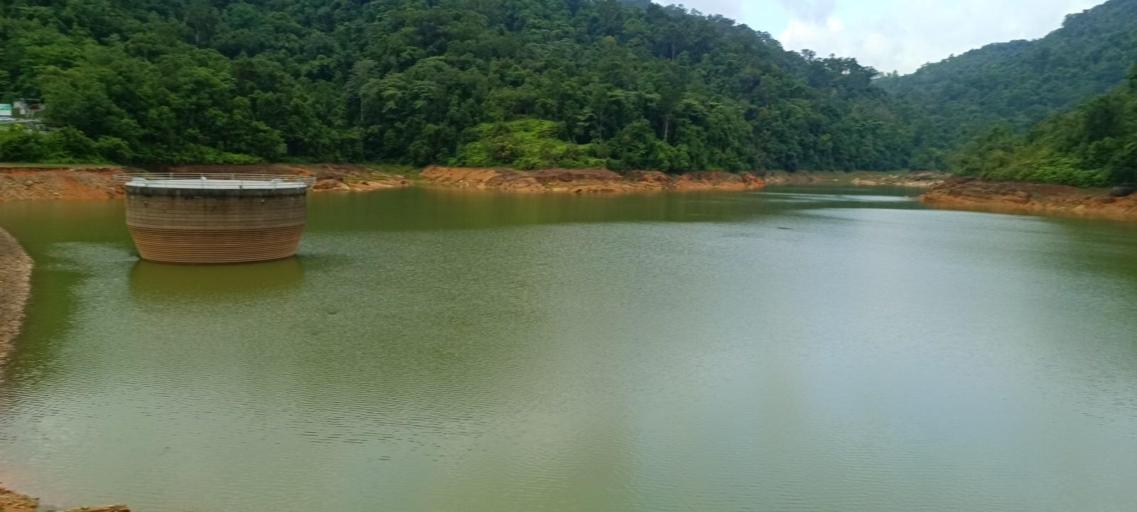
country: MY
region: Penang
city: Kampung Sungai Ara
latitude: 5.3971
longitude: 100.2627
